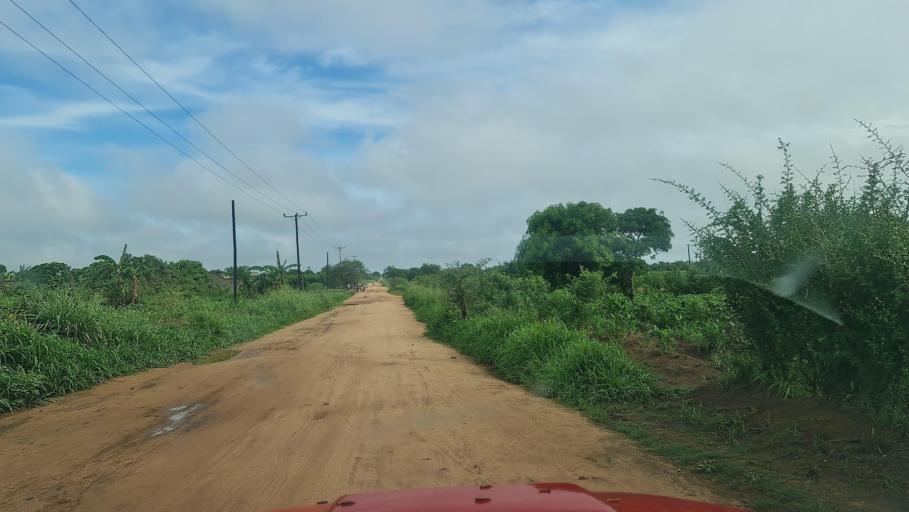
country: MW
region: Southern Region
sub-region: Nsanje District
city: Nsanje
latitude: -17.3146
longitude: 35.5924
